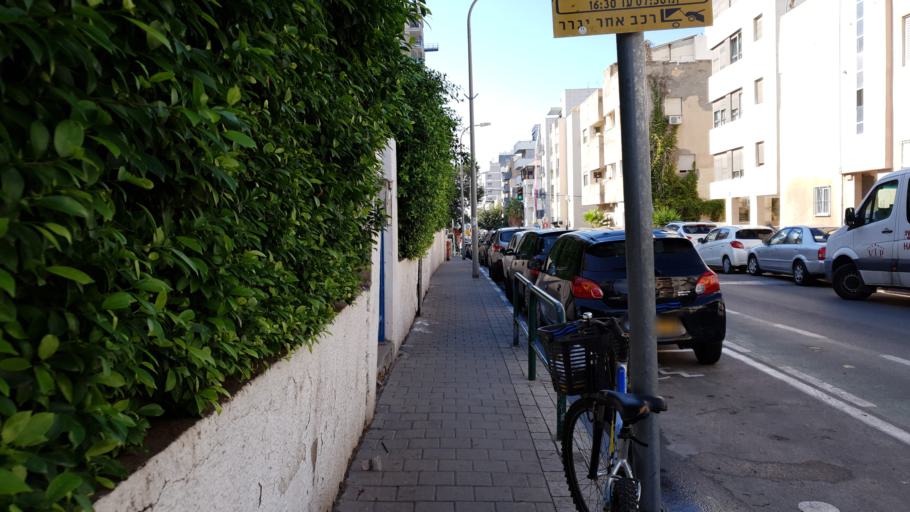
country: IL
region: Tel Aviv
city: Tel Aviv
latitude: 32.0715
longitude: 34.7681
